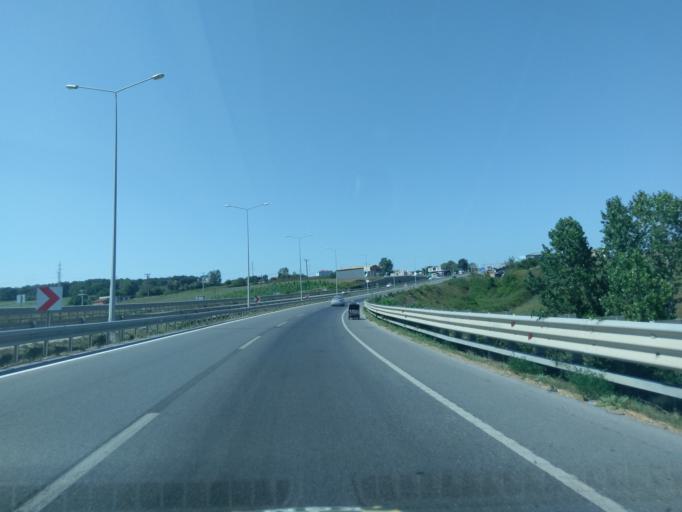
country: TR
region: Samsun
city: Bafra
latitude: 41.5420
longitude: 35.9319
